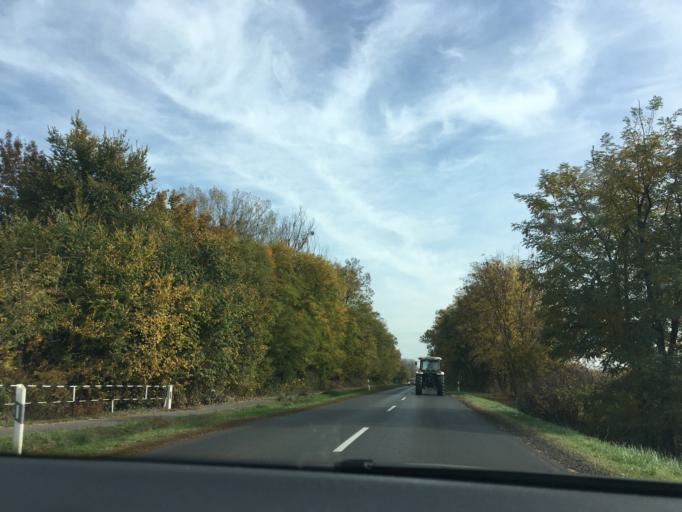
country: HU
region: Szabolcs-Szatmar-Bereg
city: Nagykallo
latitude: 47.8690
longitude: 21.8734
